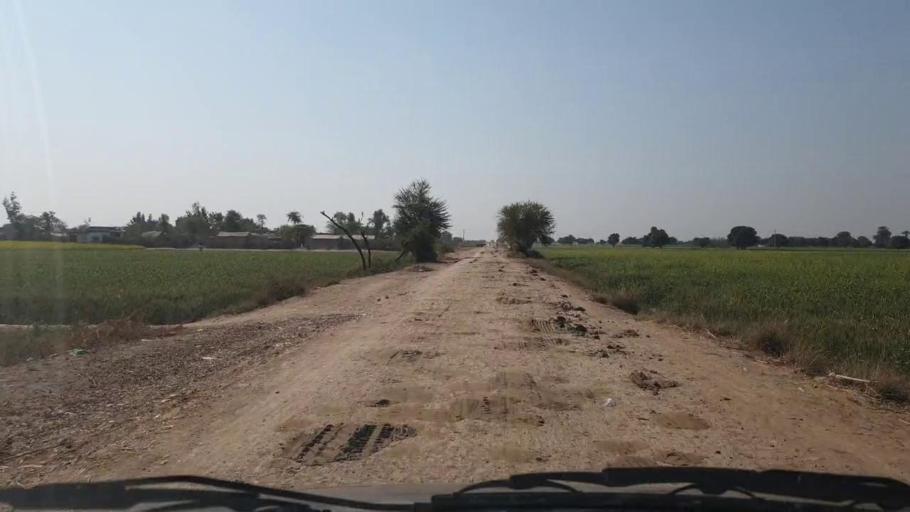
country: PK
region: Sindh
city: Samaro
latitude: 25.2740
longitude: 69.2519
